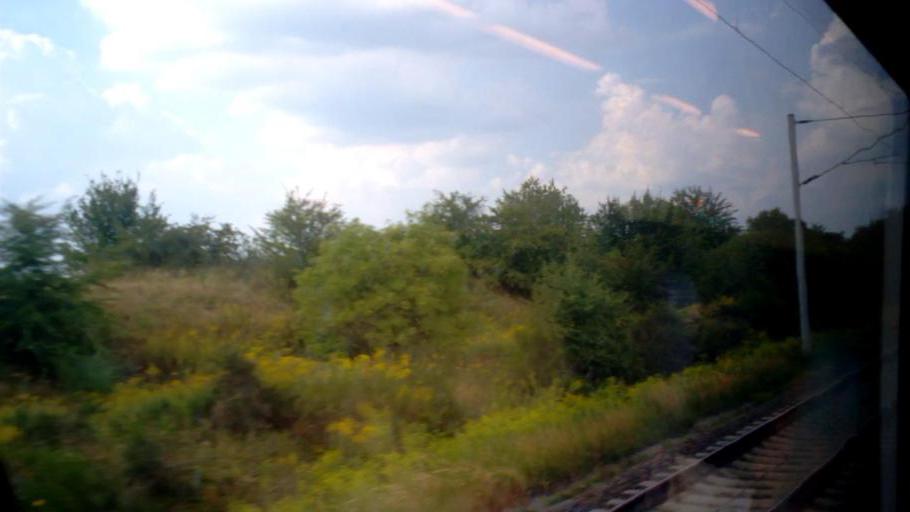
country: DE
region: Brandenburg
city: Grossbeeren
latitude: 52.3649
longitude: 13.2905
